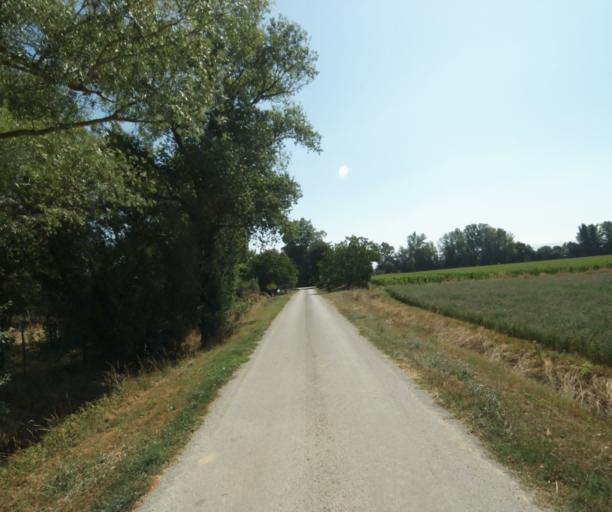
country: FR
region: Midi-Pyrenees
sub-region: Departement de la Haute-Garonne
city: Revel
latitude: 43.5063
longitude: 1.9626
